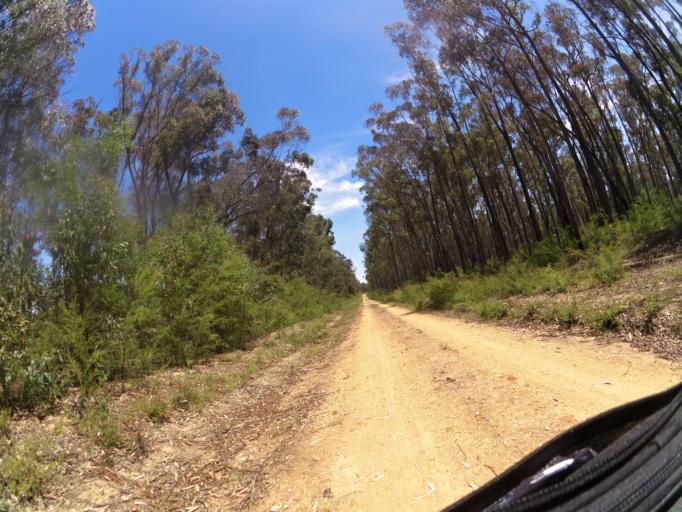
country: AU
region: Victoria
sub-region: East Gippsland
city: Lakes Entrance
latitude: -37.7573
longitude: 147.9621
